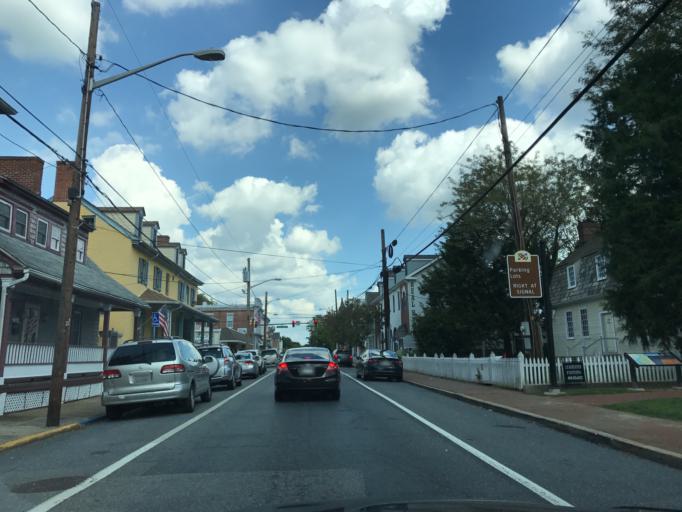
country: US
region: Maryland
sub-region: Queen Anne's County
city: Centreville
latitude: 39.0436
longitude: -76.0659
